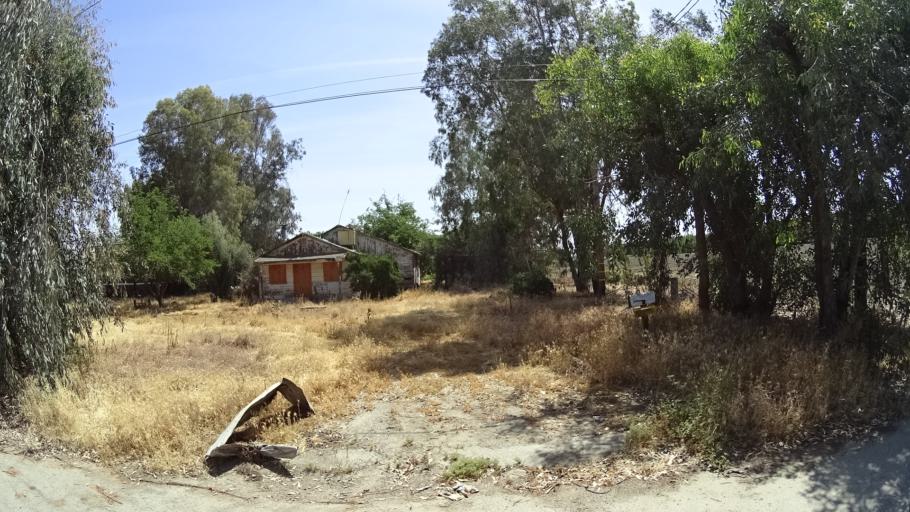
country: US
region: California
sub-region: Kings County
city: Armona
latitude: 36.3363
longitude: -119.7000
